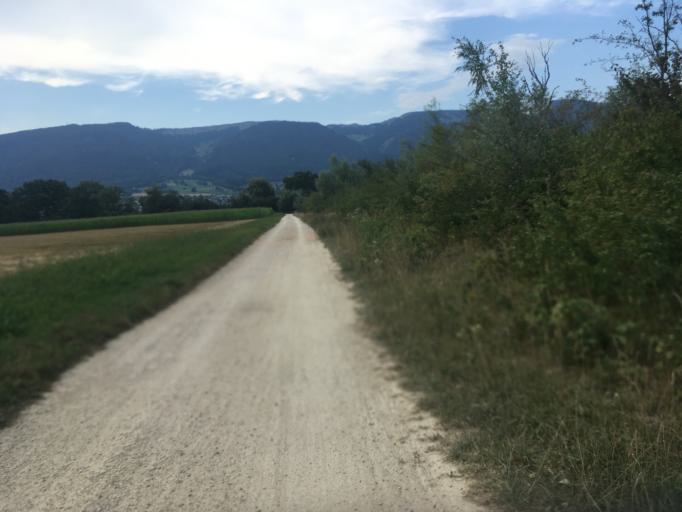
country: CH
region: Bern
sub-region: Seeland District
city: Arch
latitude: 47.1788
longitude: 7.4305
